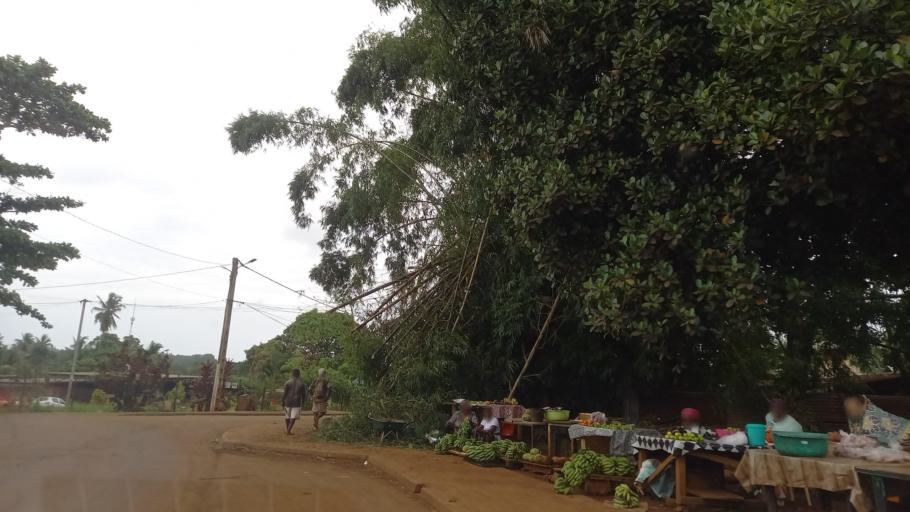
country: YT
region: Chiconi
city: Chiconi
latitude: -12.8232
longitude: 45.1300
